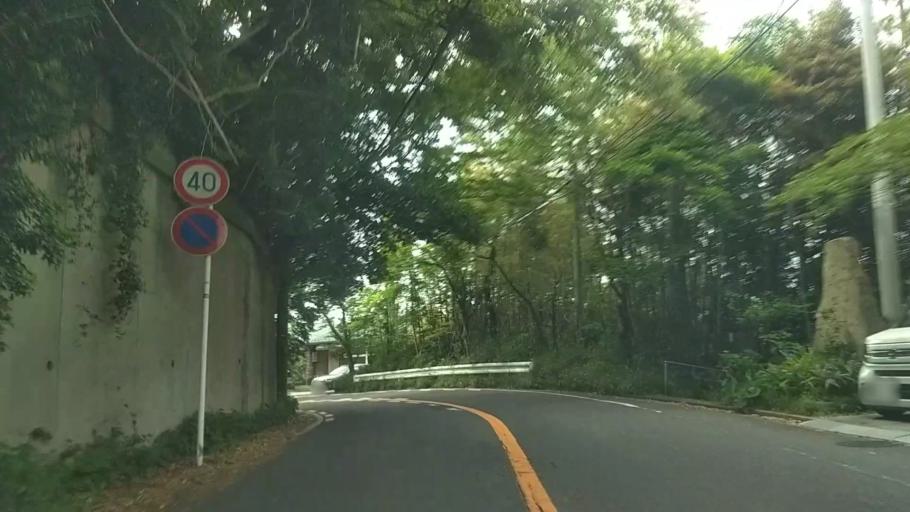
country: JP
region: Kanagawa
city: Kamakura
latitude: 35.3213
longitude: 139.5125
